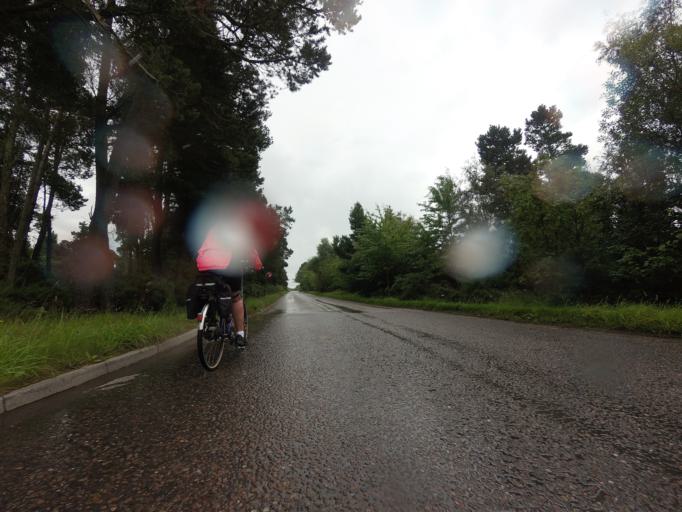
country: GB
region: Scotland
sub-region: Moray
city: Fochabers
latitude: 57.6557
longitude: -3.0573
